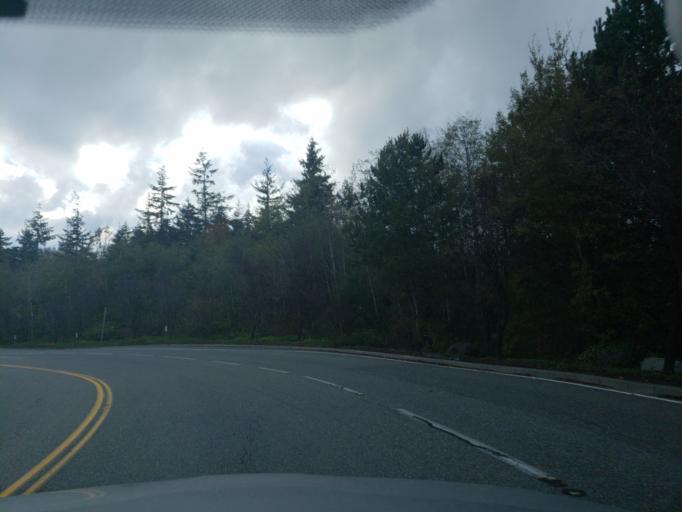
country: US
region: Washington
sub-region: Snohomish County
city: Mukilteo
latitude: 47.9327
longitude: -122.2649
